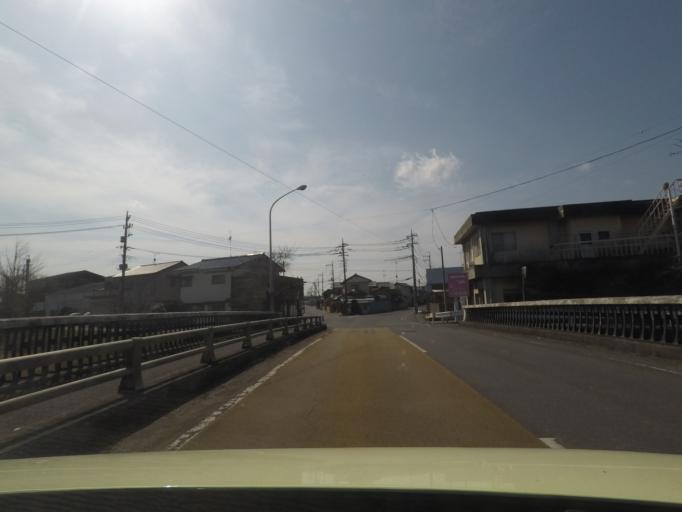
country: JP
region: Ibaraki
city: Ishioka
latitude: 36.1693
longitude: 140.3520
